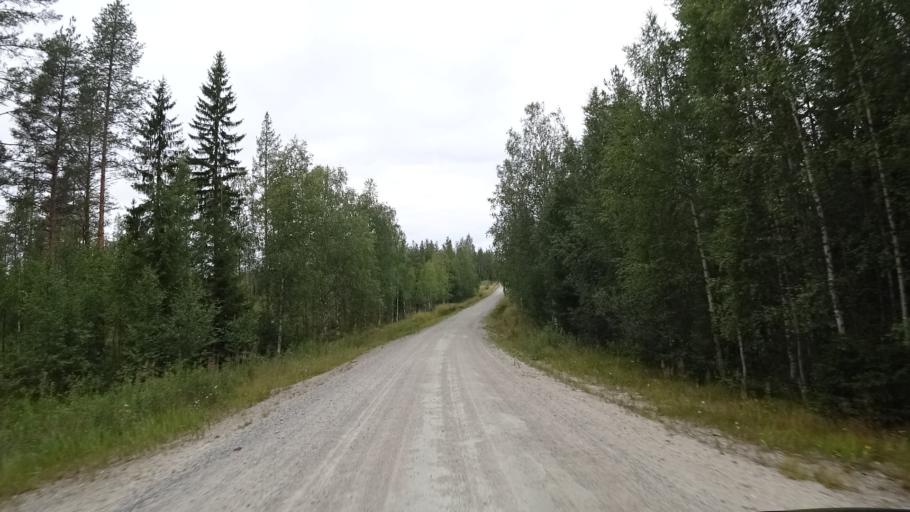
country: FI
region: North Karelia
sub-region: Joensuu
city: Eno
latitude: 63.1572
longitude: 30.5926
